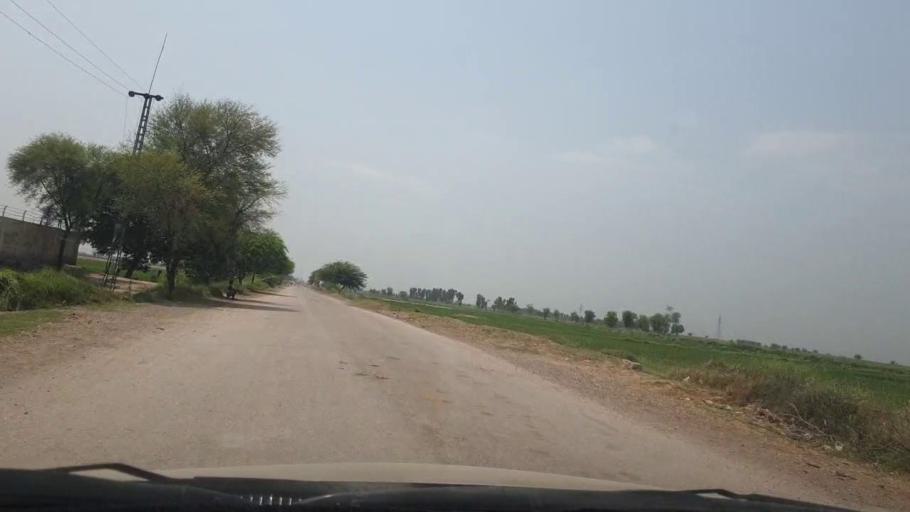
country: PK
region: Sindh
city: Ratodero
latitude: 27.7187
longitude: 68.2785
